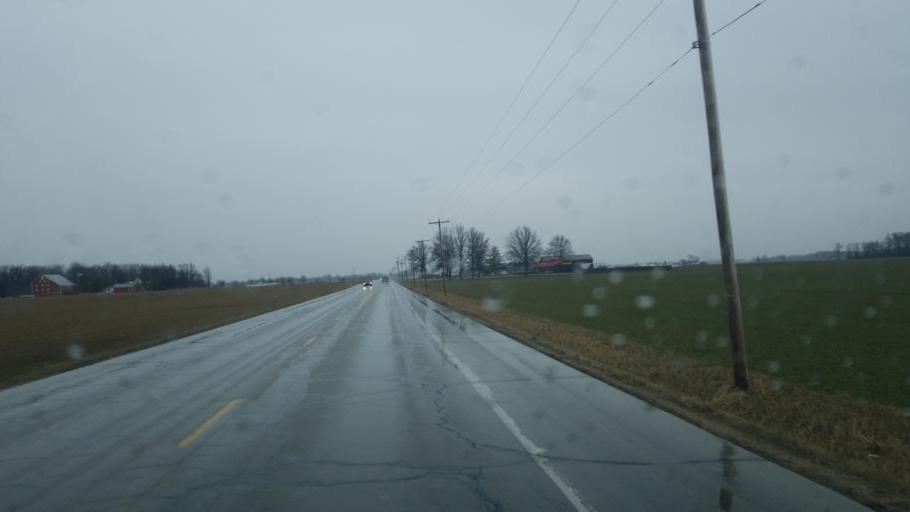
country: US
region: Indiana
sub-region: Adams County
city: Berne
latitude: 40.6855
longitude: -84.9556
